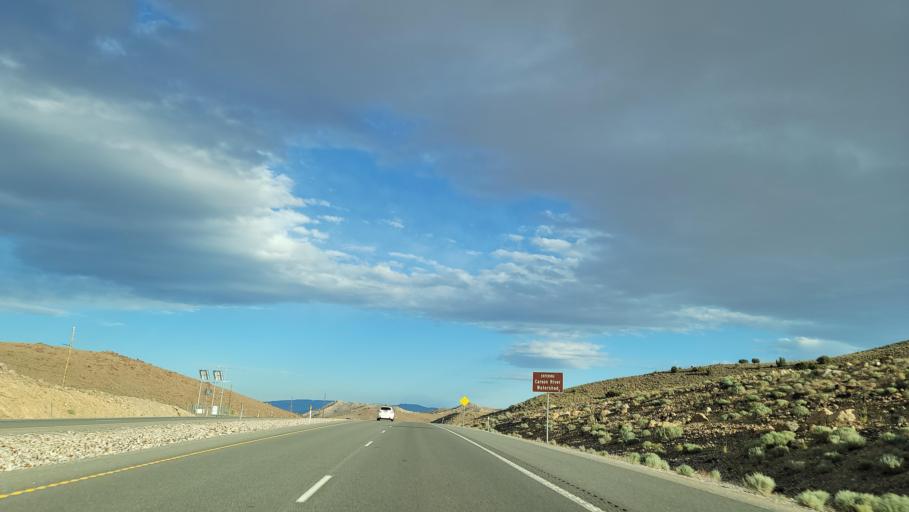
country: US
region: Nevada
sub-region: Lyon County
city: Stagecoach
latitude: 39.4784
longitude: -119.4010
